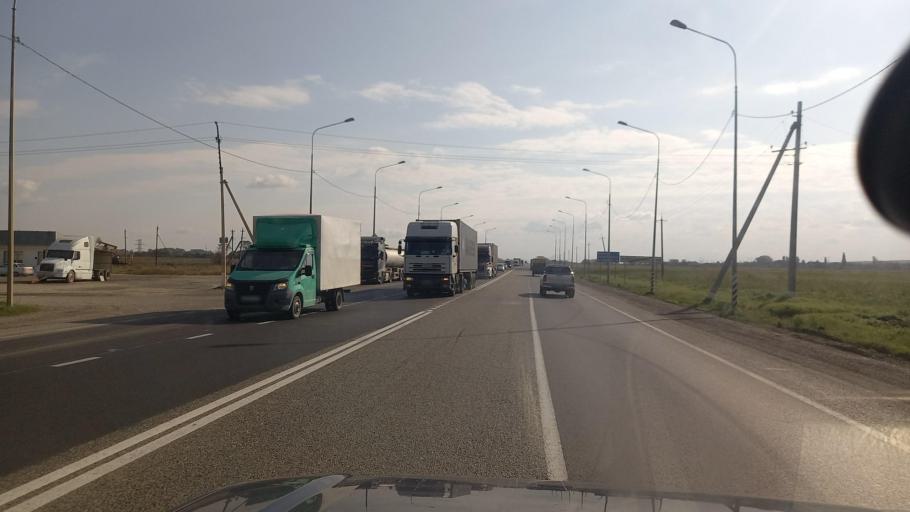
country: RU
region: Krasnodarskiy
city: Novoukrainskiy
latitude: 44.8937
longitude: 38.0636
